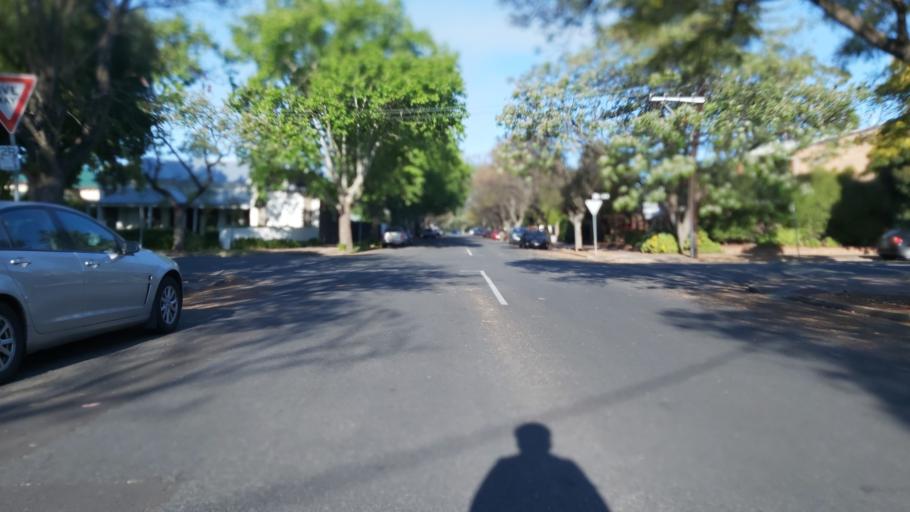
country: AU
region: South Australia
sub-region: Unley
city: Unley
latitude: -34.9438
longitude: 138.5960
